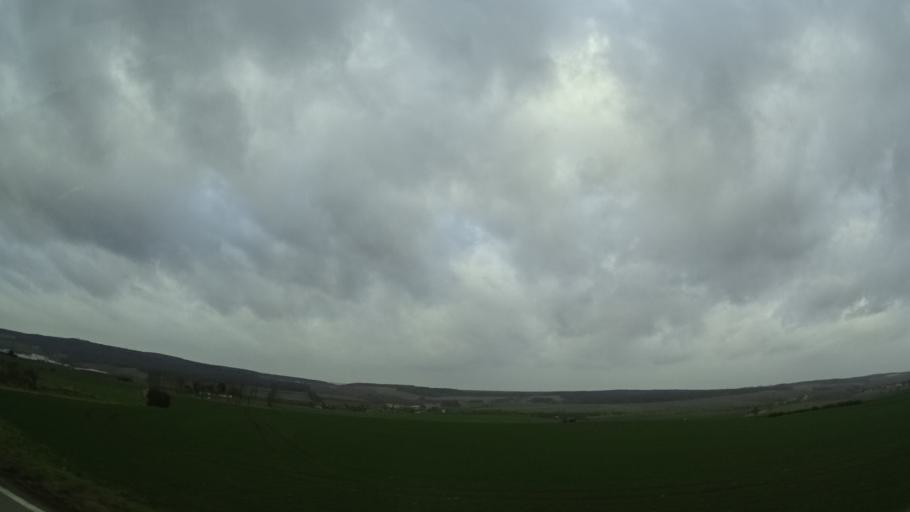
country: DE
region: Thuringia
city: Schmieritz
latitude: 50.7242
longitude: 11.7964
